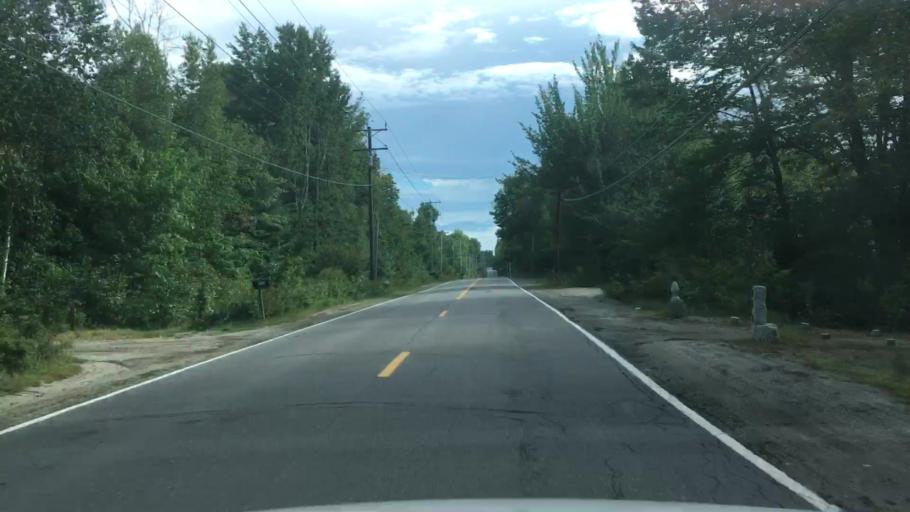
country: US
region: Maine
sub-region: Hancock County
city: Ellsworth
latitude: 44.4957
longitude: -68.4203
